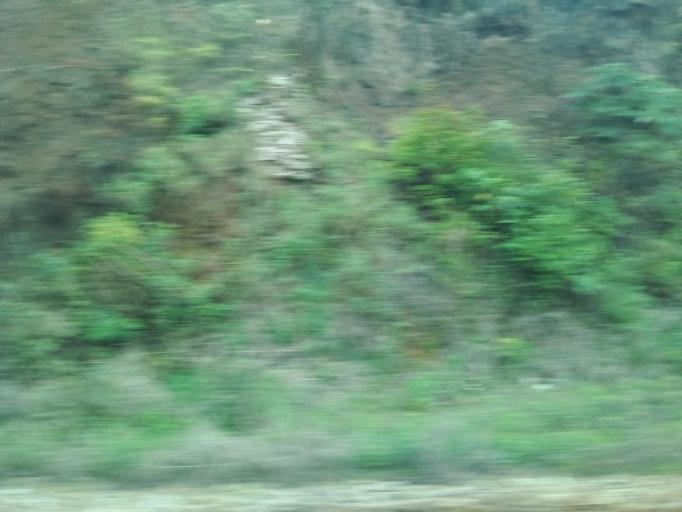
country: BR
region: Minas Gerais
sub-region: Rio Piracicaba
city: Rio Piracicaba
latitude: -19.9637
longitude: -43.2689
